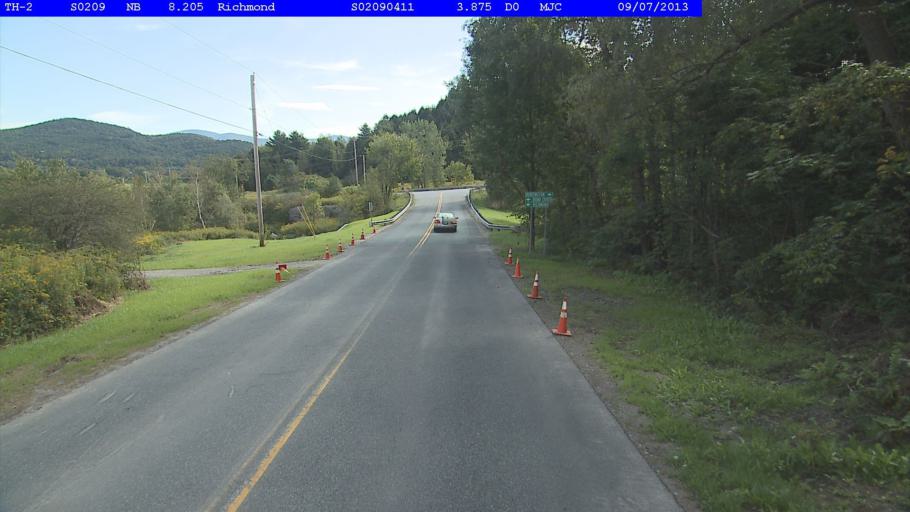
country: US
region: Vermont
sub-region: Chittenden County
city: Williston
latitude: 44.3980
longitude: -73.0139
